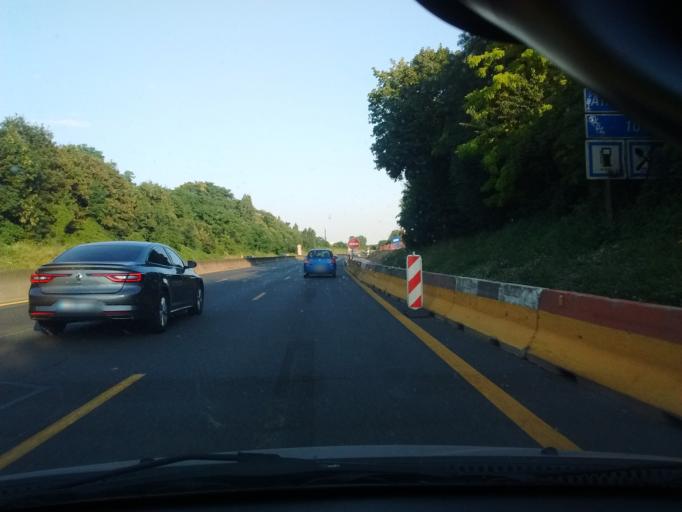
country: FR
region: Ile-de-France
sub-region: Departement de l'Essonne
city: Grigny
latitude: 48.6585
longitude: 2.3750
